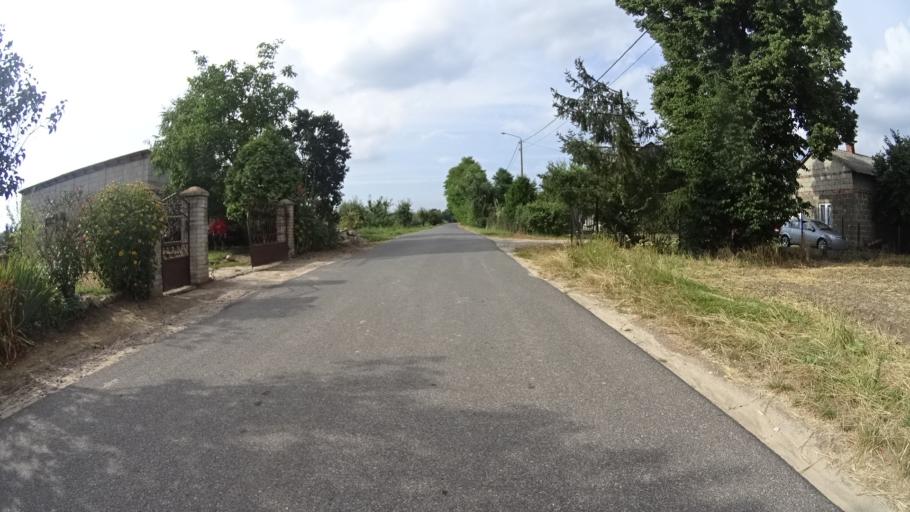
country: PL
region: Masovian Voivodeship
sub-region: Powiat grojecki
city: Goszczyn
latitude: 51.7055
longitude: 20.8439
